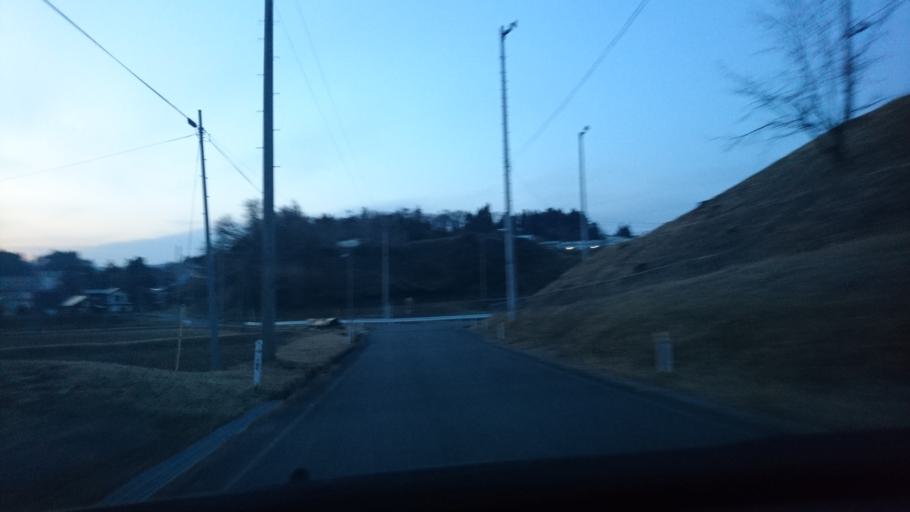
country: JP
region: Iwate
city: Ichinoseki
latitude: 38.9100
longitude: 141.3458
